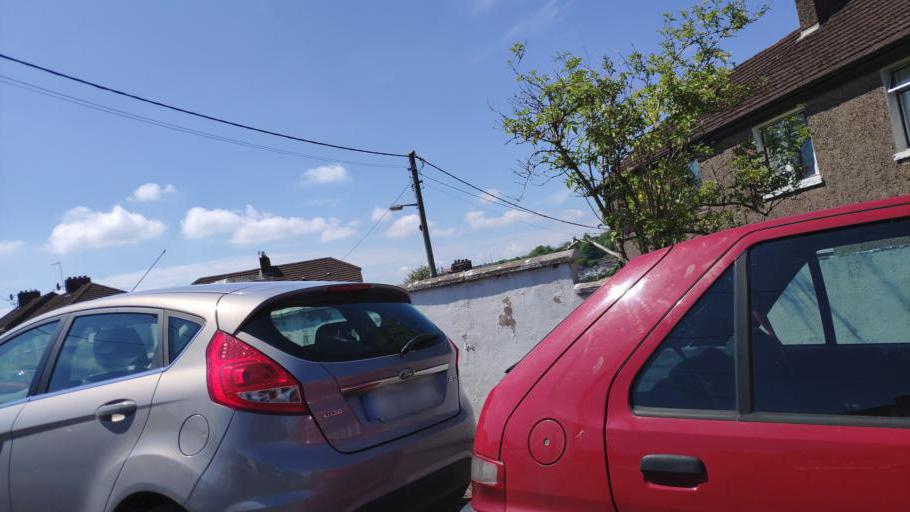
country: IE
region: Munster
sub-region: County Cork
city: Cork
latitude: 51.9114
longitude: -8.4698
